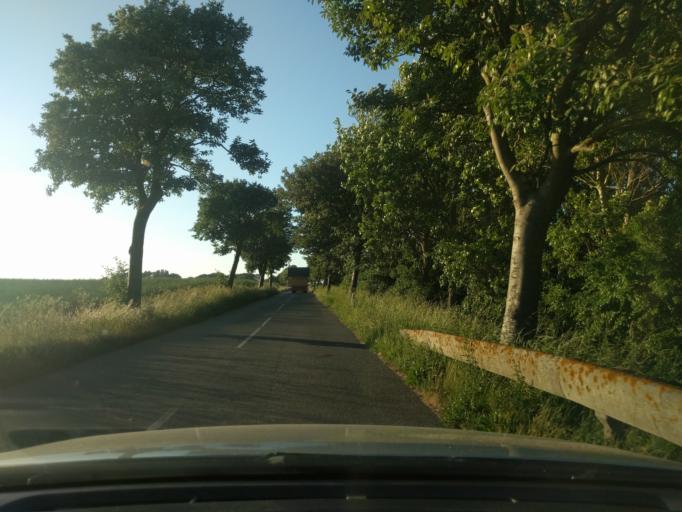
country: DK
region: South Denmark
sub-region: Kerteminde Kommune
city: Kerteminde
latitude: 55.5878
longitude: 10.6308
